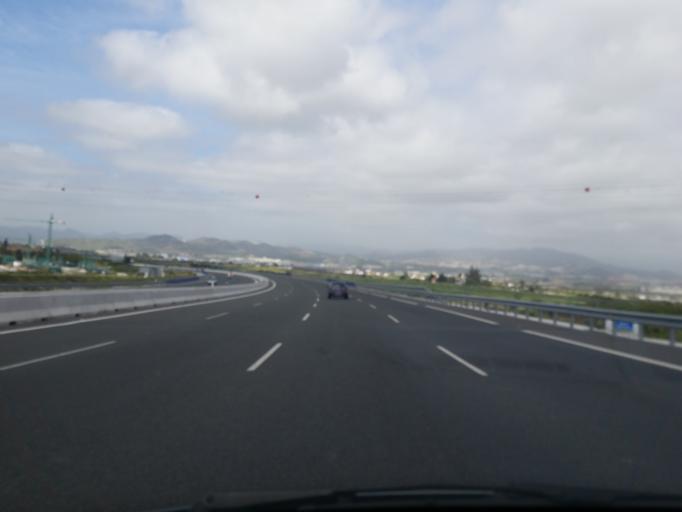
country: ES
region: Andalusia
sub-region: Provincia de Malaga
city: Alhaurin de la Torre
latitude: 36.6753
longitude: -4.5266
